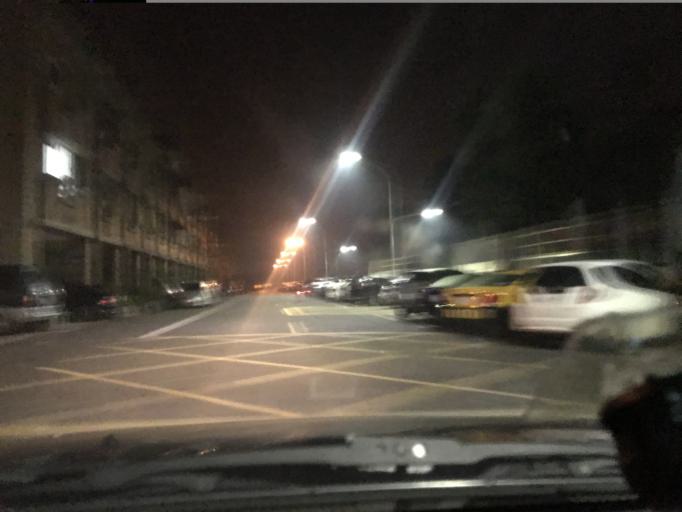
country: TW
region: Taiwan
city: Daxi
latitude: 24.9171
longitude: 121.2483
